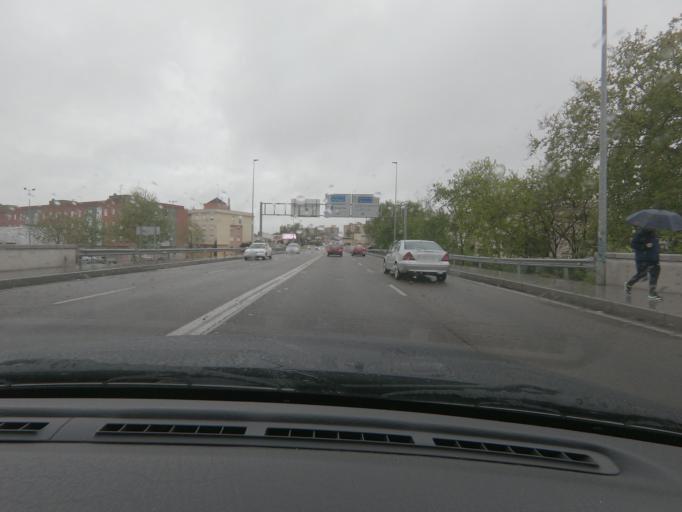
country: ES
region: Extremadura
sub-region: Provincia de Badajoz
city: Badajoz
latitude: 38.8828
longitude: -6.9844
